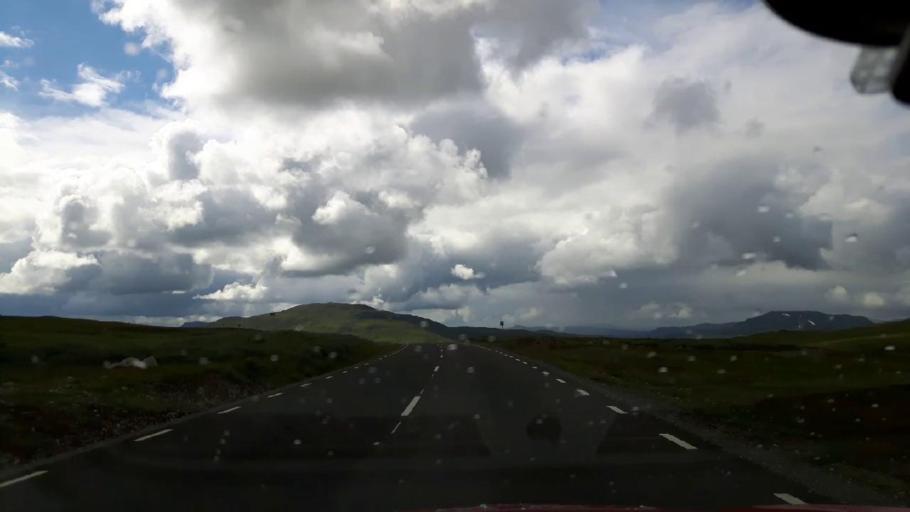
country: NO
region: Nordland
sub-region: Hattfjelldal
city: Hattfjelldal
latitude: 65.0449
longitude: 14.3318
